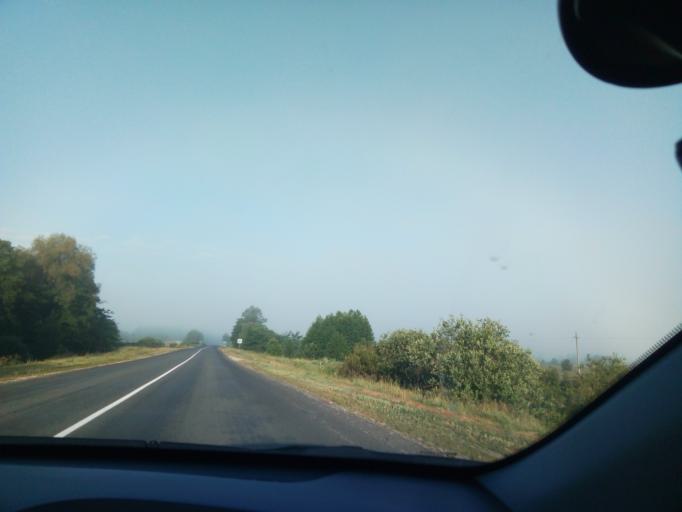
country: RU
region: Nizjnij Novgorod
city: Voznesenskoye
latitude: 54.8664
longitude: 42.9510
